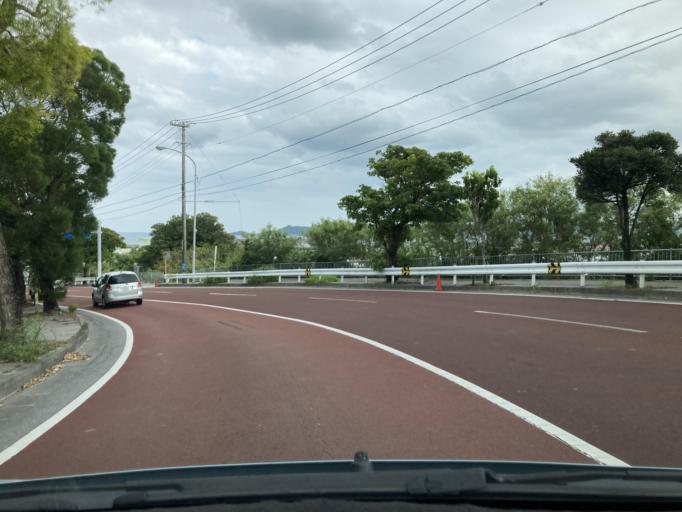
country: JP
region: Okinawa
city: Ginowan
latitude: 26.2317
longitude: 127.7671
